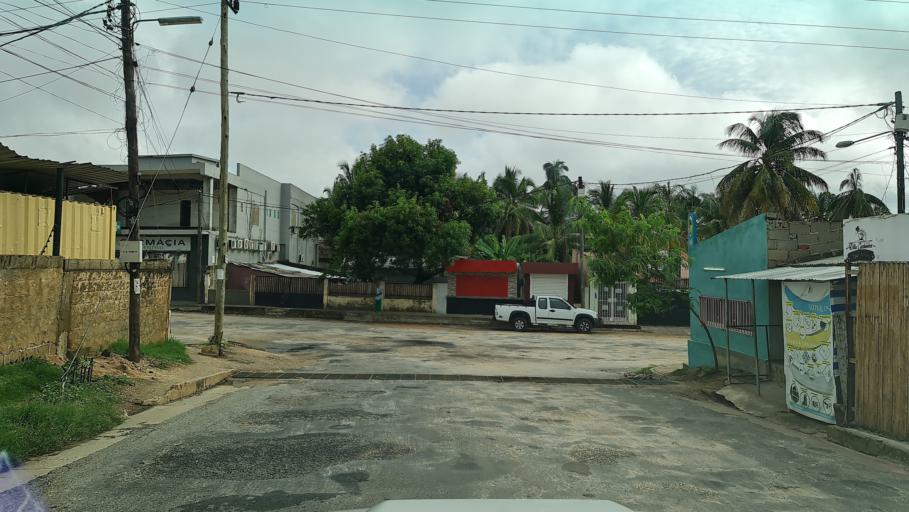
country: MZ
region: Nampula
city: Nampula
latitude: -15.1267
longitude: 39.2641
